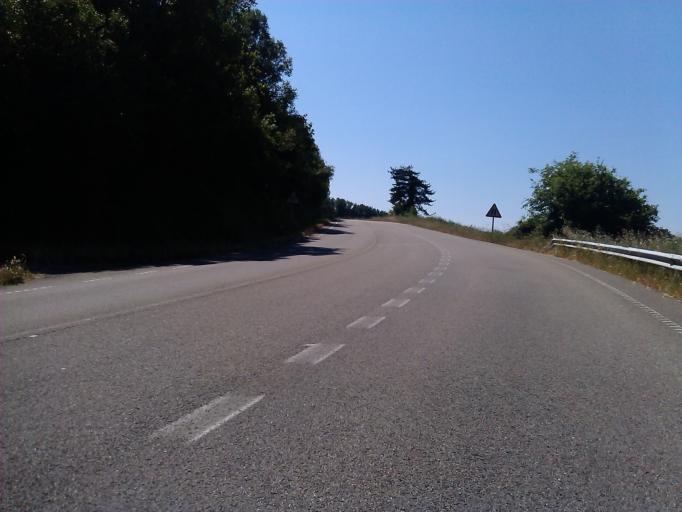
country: ES
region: Galicia
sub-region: Provincia de Lugo
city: Samos
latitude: 42.7345
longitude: -7.3560
